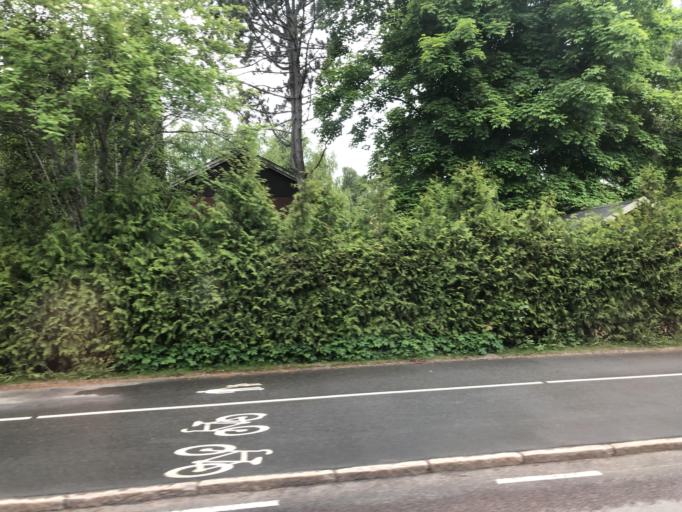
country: SE
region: Stockholm
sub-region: Huddinge Kommun
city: Huddinge
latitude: 59.2489
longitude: 17.9665
